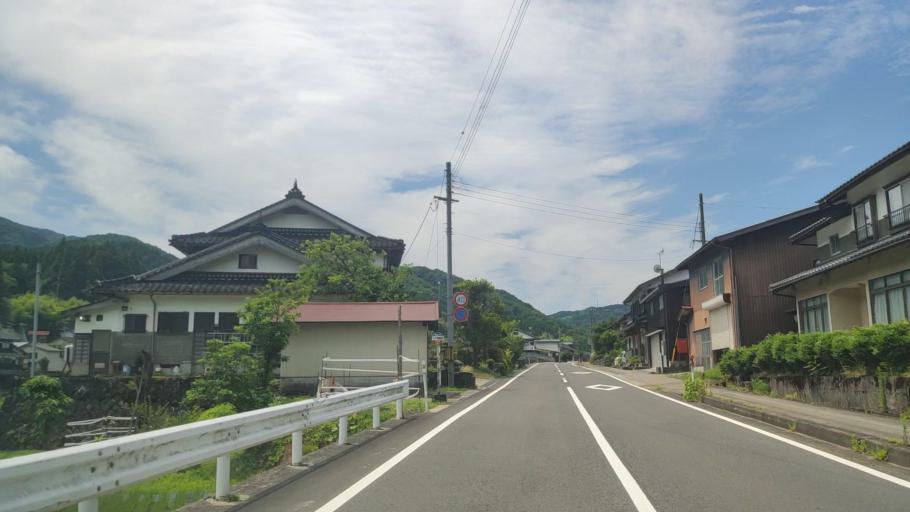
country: JP
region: Hyogo
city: Toyooka
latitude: 35.4679
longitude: 134.5482
